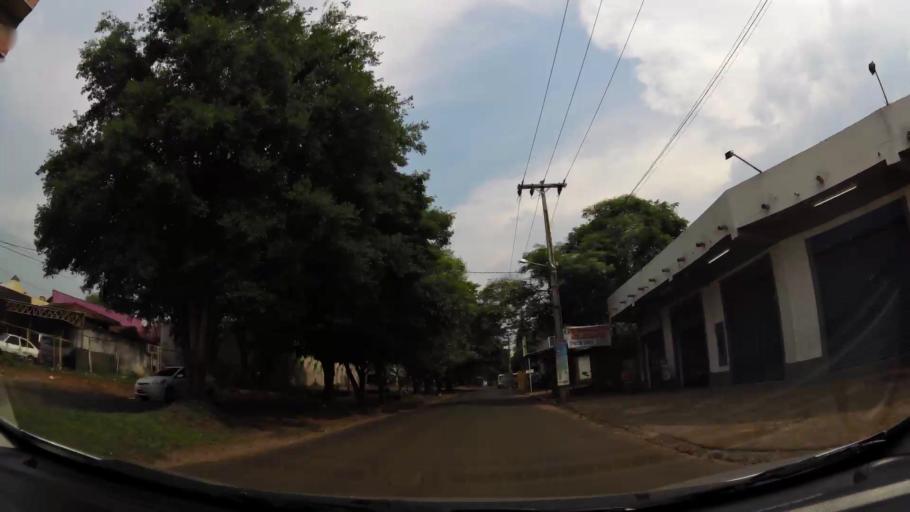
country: PY
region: Alto Parana
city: Presidente Franco
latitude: -25.5373
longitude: -54.6065
